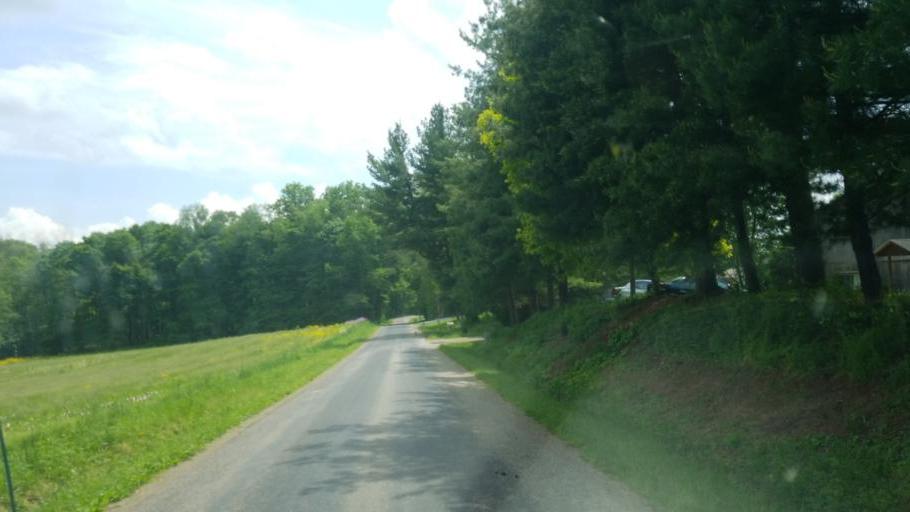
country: US
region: Ohio
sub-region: Ashland County
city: Ashland
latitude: 40.7716
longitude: -82.3396
